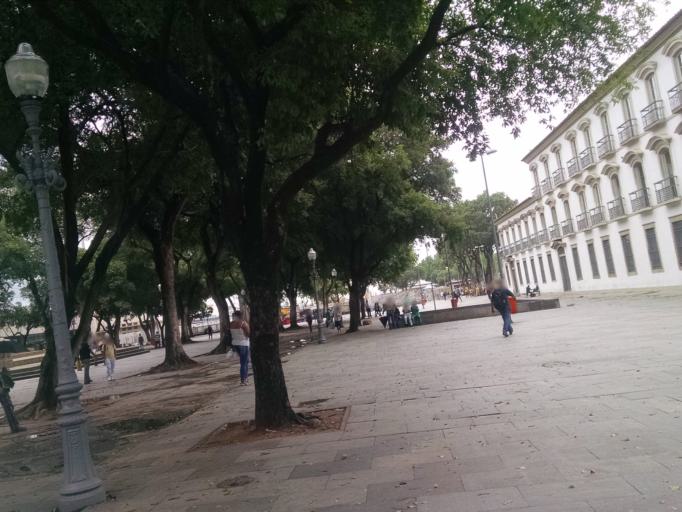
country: BR
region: Rio de Janeiro
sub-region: Rio De Janeiro
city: Rio de Janeiro
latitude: -22.9036
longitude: -43.1749
